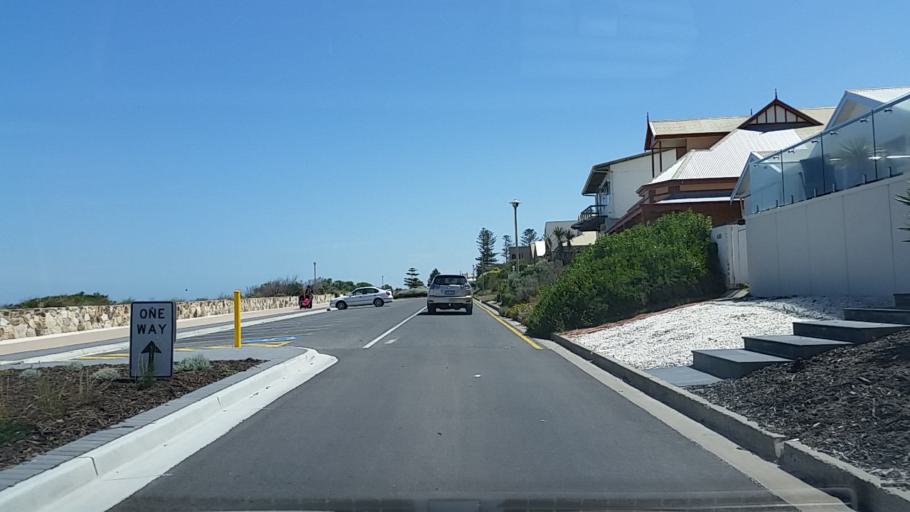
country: AU
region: South Australia
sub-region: Charles Sturt
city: Grange
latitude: -34.9074
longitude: 138.4903
